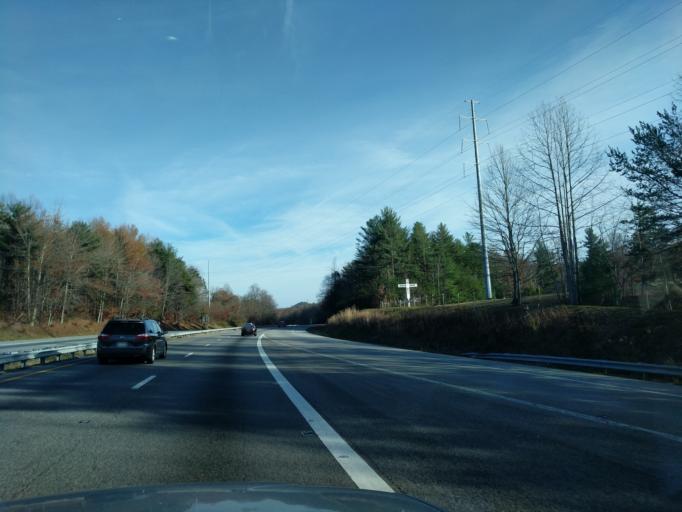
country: US
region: North Carolina
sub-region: Henderson County
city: Dana
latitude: 35.2485
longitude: -82.3252
